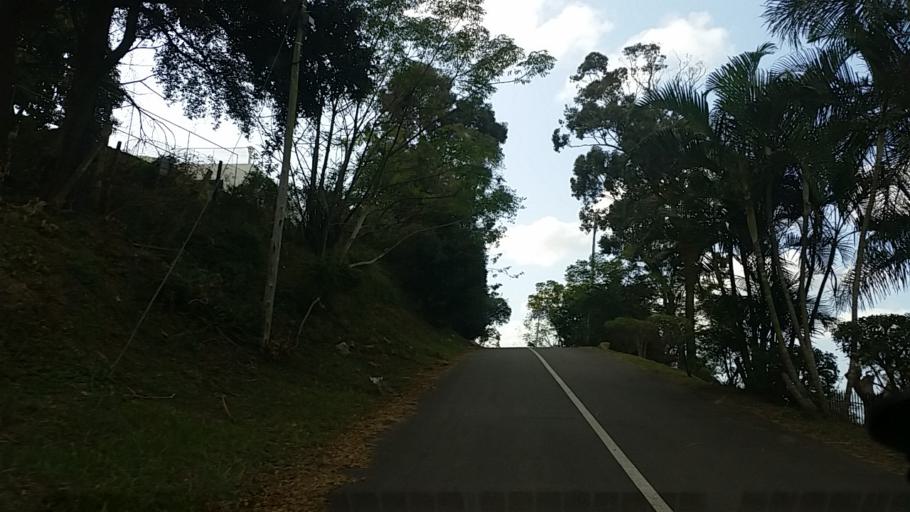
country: ZA
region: KwaZulu-Natal
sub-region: eThekwini Metropolitan Municipality
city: Berea
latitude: -29.8345
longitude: 30.9439
